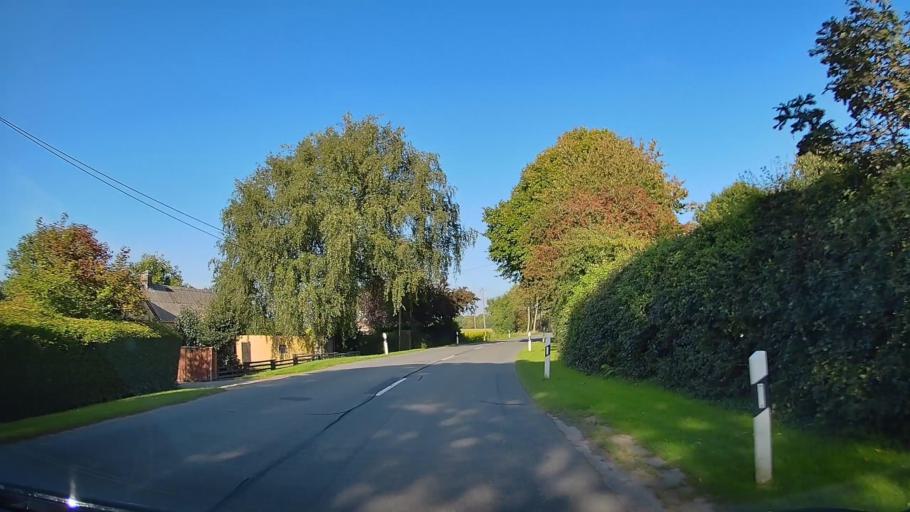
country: DE
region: Lower Saxony
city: Cappel
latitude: 53.7601
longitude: 8.5626
